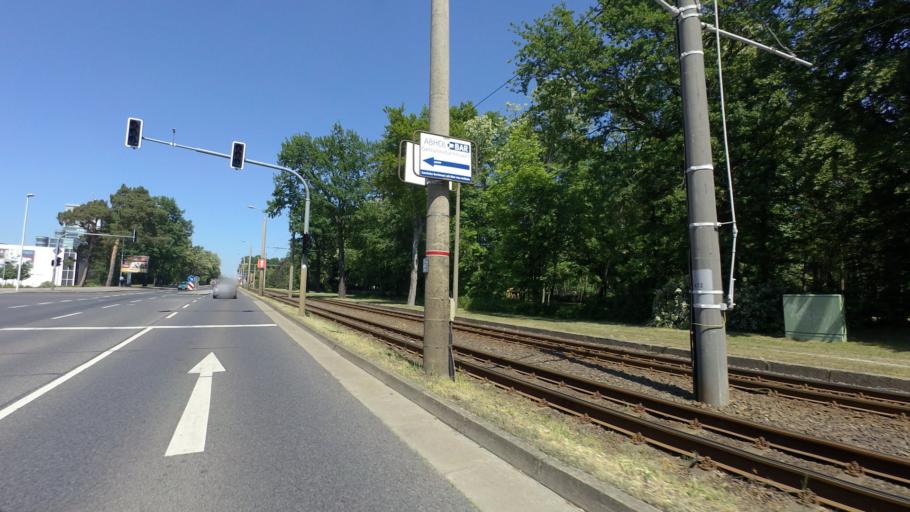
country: DE
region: Brandenburg
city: Cottbus
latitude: 51.7344
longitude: 14.3378
